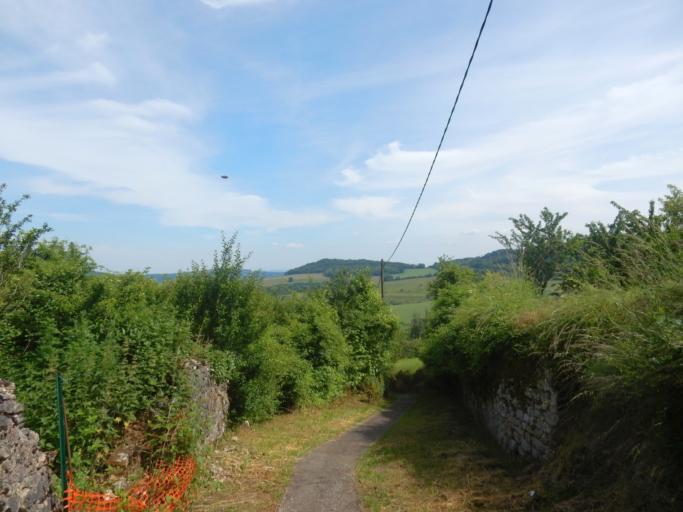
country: FR
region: Lorraine
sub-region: Departement de Meurthe-et-Moselle
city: Pagny-sur-Moselle
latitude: 48.9773
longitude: 5.9962
